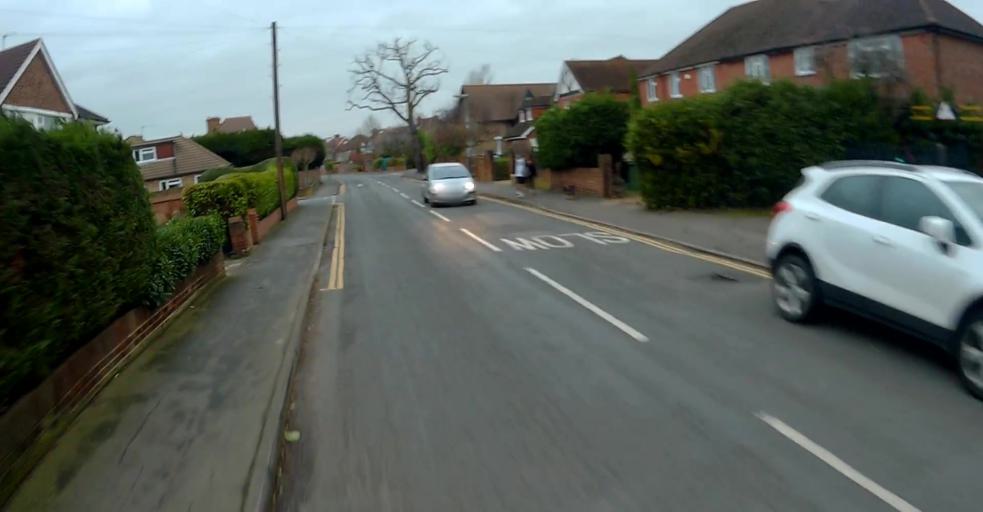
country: GB
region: England
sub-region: Surrey
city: Walton-on-Thames
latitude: 51.3830
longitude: -0.4073
